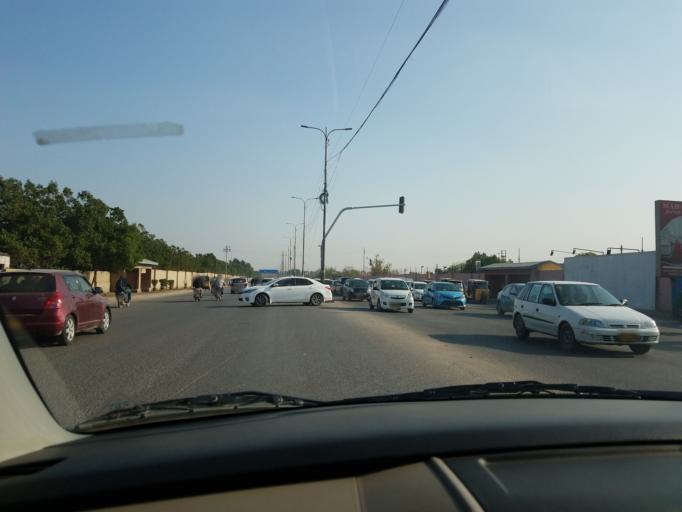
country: PK
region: Sindh
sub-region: Karachi District
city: Karachi
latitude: 24.8922
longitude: 67.1217
